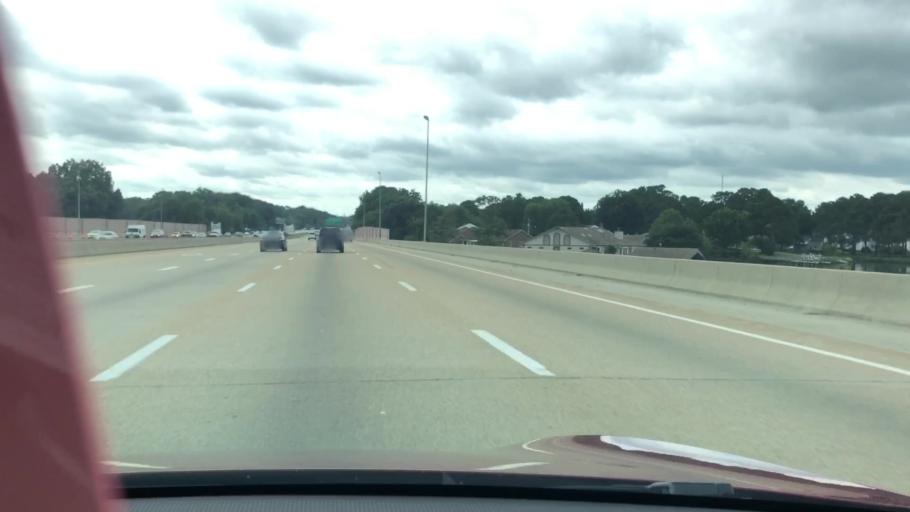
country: US
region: Virginia
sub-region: City of Chesapeake
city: Chesapeake
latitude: 36.8289
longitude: -76.1958
